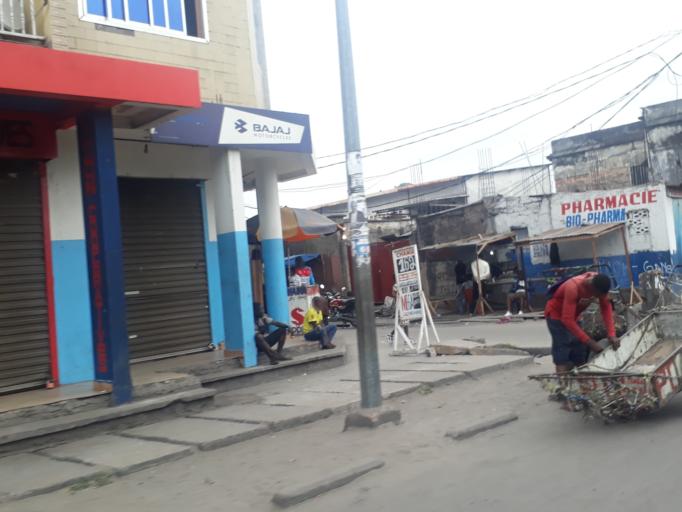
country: CD
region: Kinshasa
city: Kinshasa
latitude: -4.3160
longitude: 15.3102
